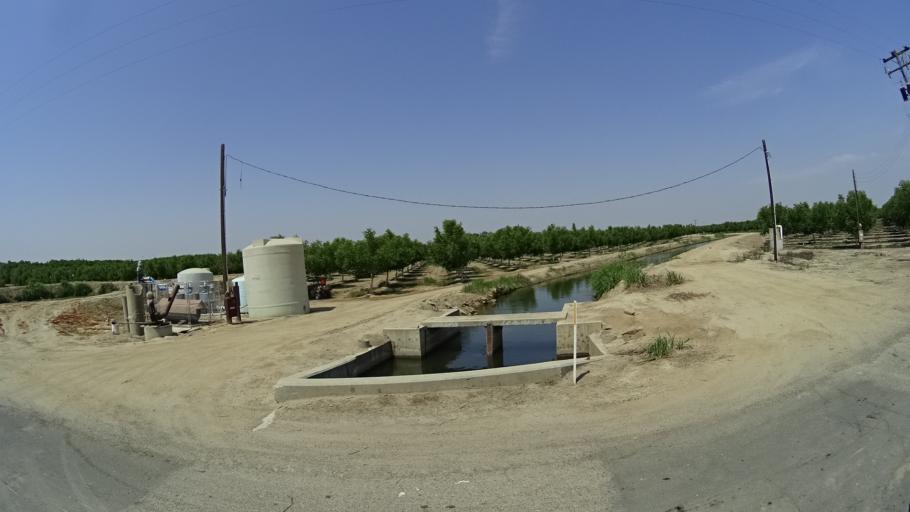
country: US
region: California
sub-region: Kings County
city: Lemoore
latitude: 36.3442
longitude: -119.7628
